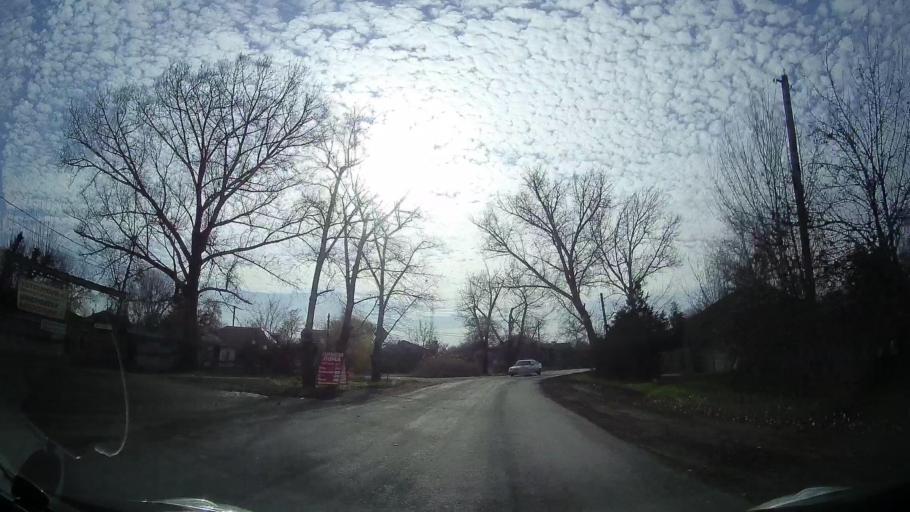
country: RU
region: Rostov
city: Veselyy
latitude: 47.0870
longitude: 40.7383
